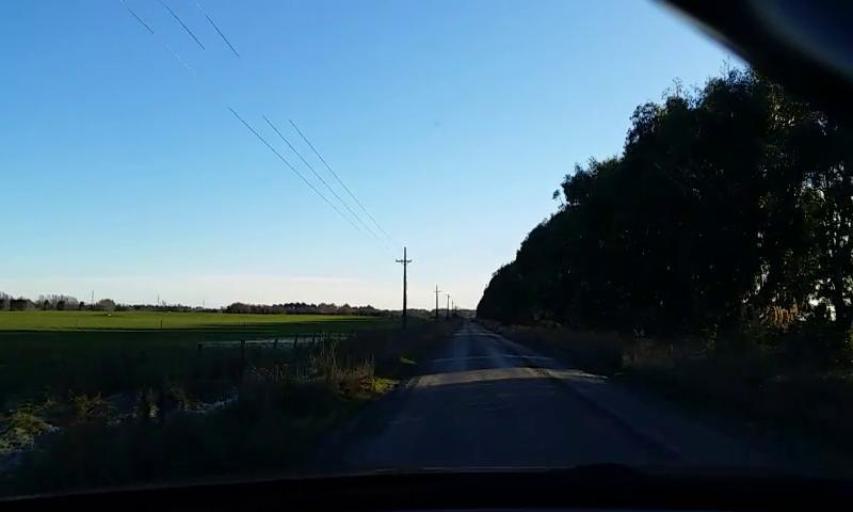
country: NZ
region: Southland
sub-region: Invercargill City
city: Invercargill
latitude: -46.2918
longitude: 168.4424
